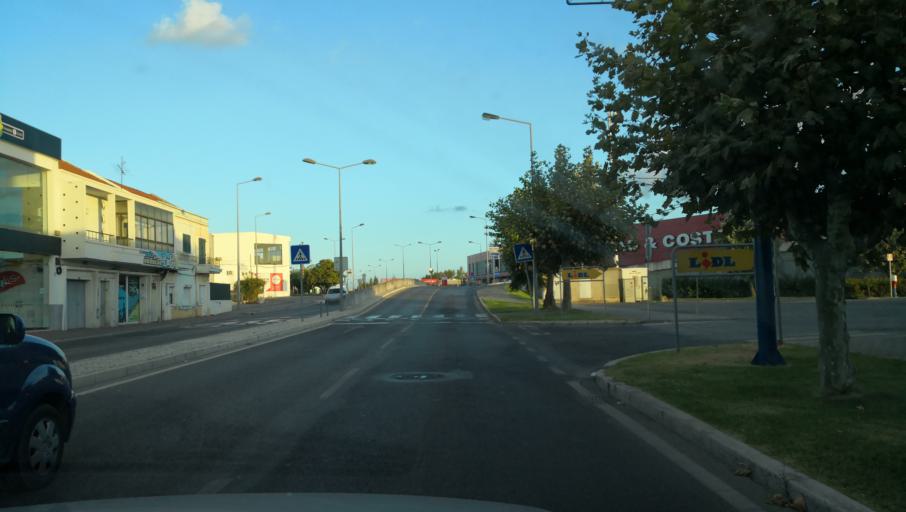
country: PT
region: Setubal
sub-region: Moita
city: Alhos Vedros
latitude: 38.6568
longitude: -9.0364
